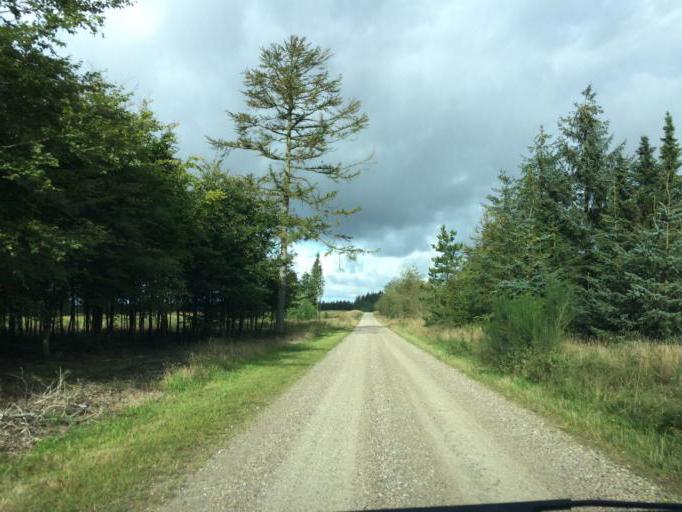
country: DK
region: Central Jutland
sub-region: Holstebro Kommune
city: Ulfborg
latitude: 56.2707
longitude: 8.4114
